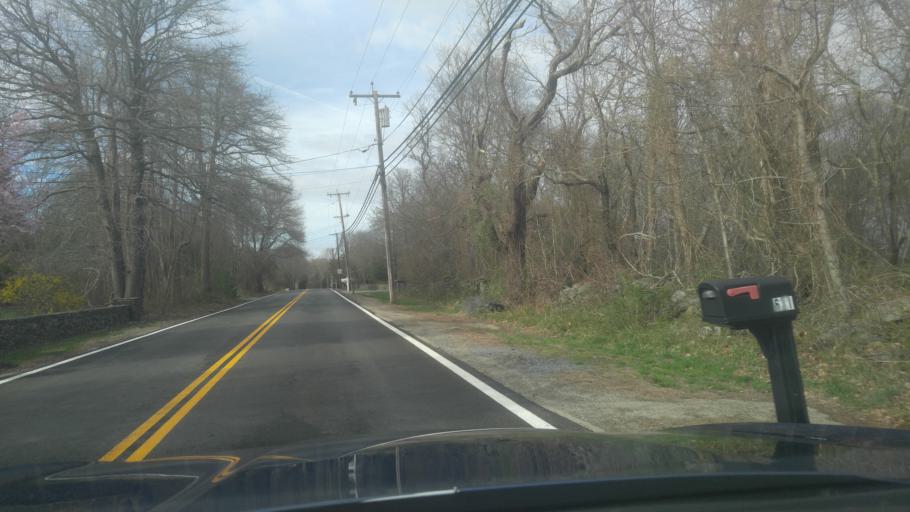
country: US
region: Rhode Island
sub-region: Newport County
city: Jamestown
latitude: 41.5472
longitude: -71.3638
